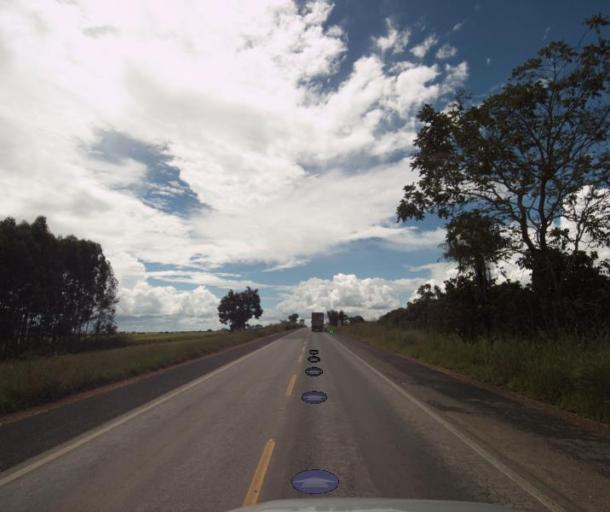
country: BR
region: Goias
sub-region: Uruacu
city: Uruacu
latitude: -14.1669
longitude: -49.1240
